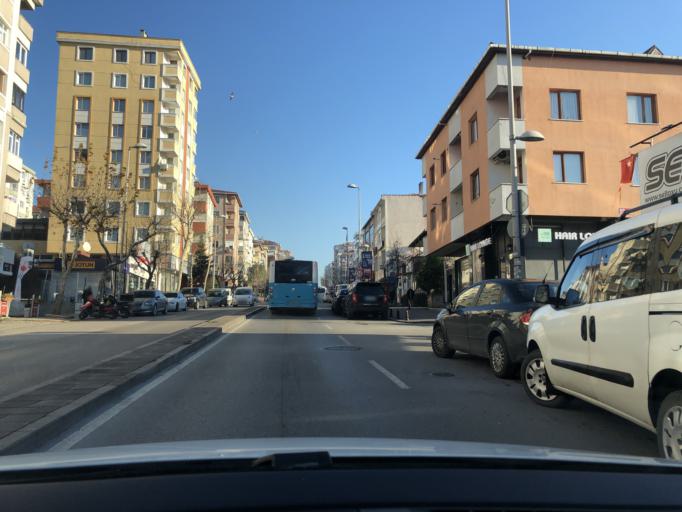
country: TR
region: Istanbul
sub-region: Atasehir
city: Atasehir
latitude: 40.9730
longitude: 29.1192
